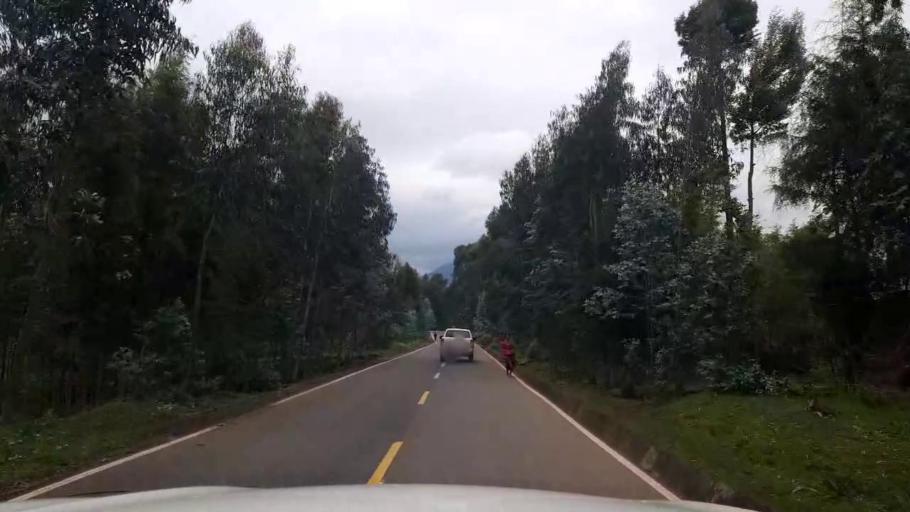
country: RW
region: Northern Province
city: Musanze
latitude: -1.4371
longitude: 29.5497
